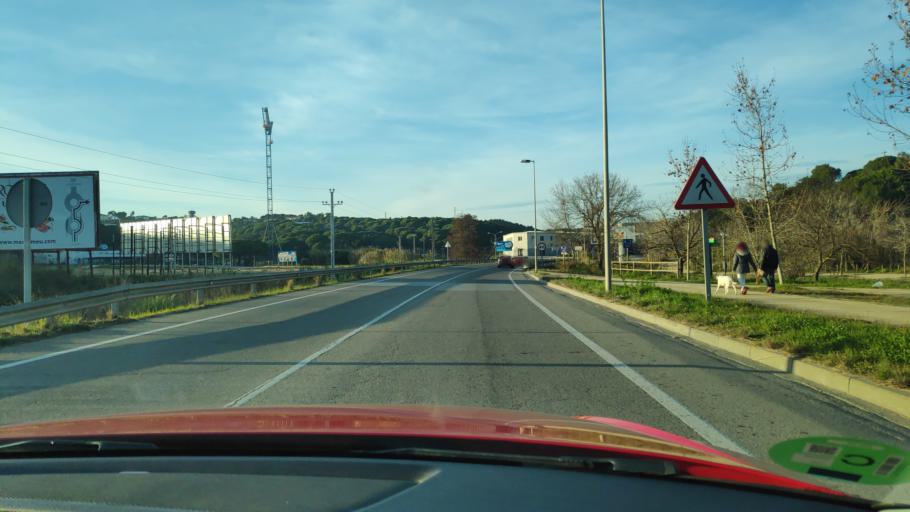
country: ES
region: Catalonia
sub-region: Provincia de Girona
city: Lloret de Mar
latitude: 41.7078
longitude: 2.8337
